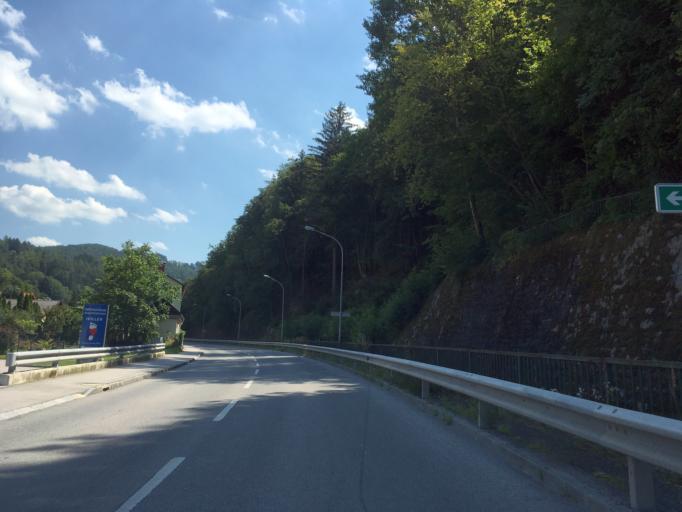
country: AT
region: Lower Austria
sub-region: Politischer Bezirk Neunkirchen
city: Edlitz
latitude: 47.5972
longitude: 16.1399
